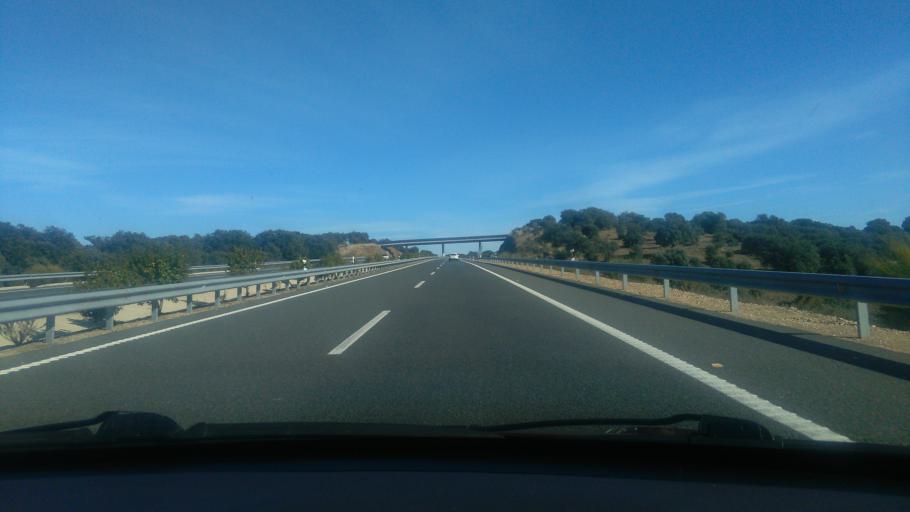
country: ES
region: Extremadura
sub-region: Provincia de Caceres
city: Plasenzuela
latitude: 39.4372
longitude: -6.0824
